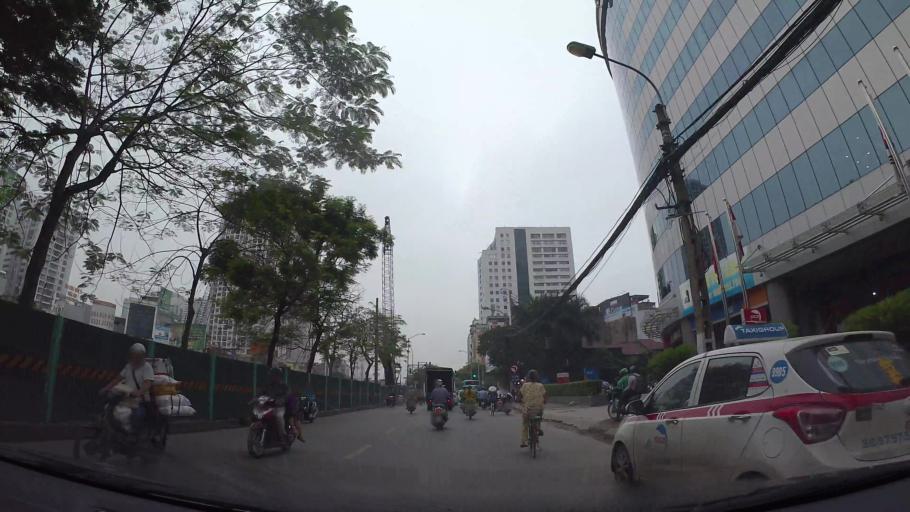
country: VN
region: Ha Noi
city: Hai BaTrung
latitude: 20.9970
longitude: 105.8619
